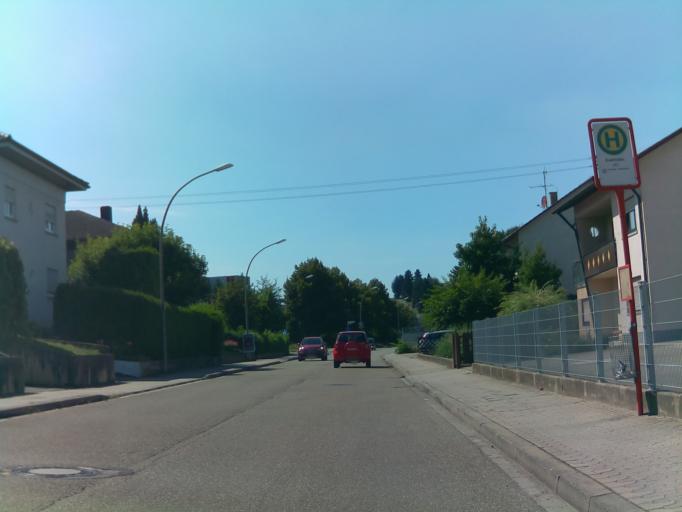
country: DE
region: Baden-Wuerttemberg
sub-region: Karlsruhe Region
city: Oberderdingen
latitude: 49.0871
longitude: 8.7736
